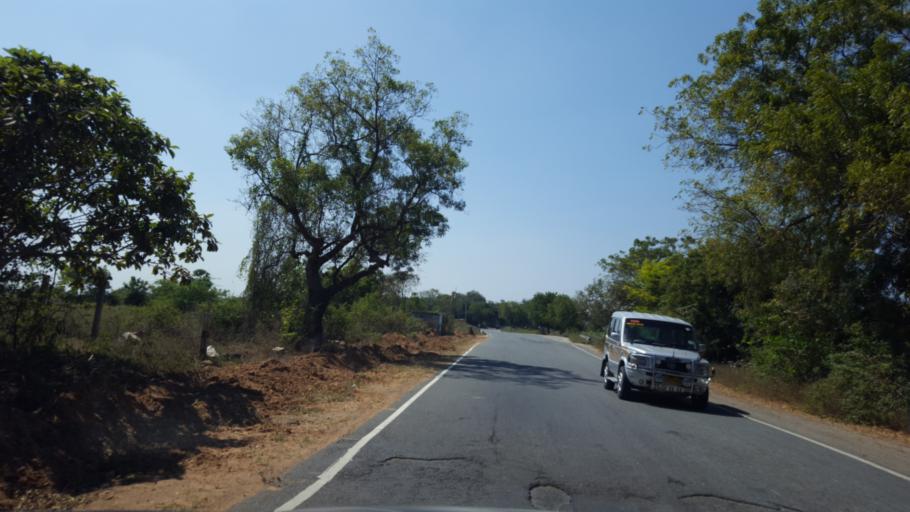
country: IN
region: Tamil Nadu
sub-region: Kancheepuram
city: Wallajahbad
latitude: 12.7740
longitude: 79.8853
